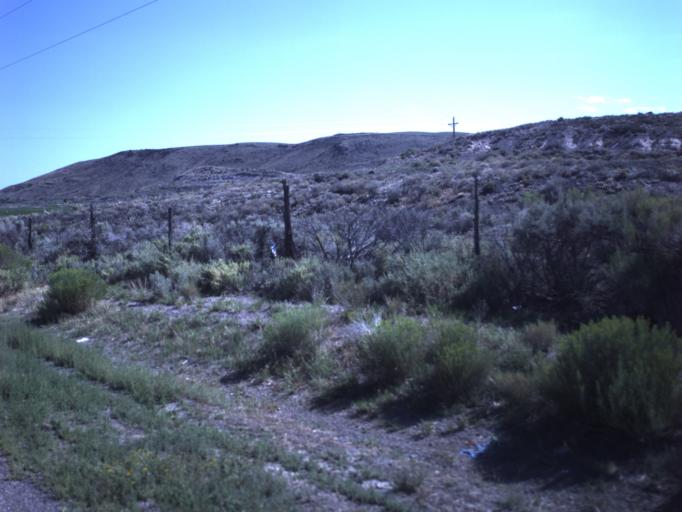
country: US
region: Utah
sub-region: Wayne County
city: Loa
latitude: 38.4179
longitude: -111.6202
